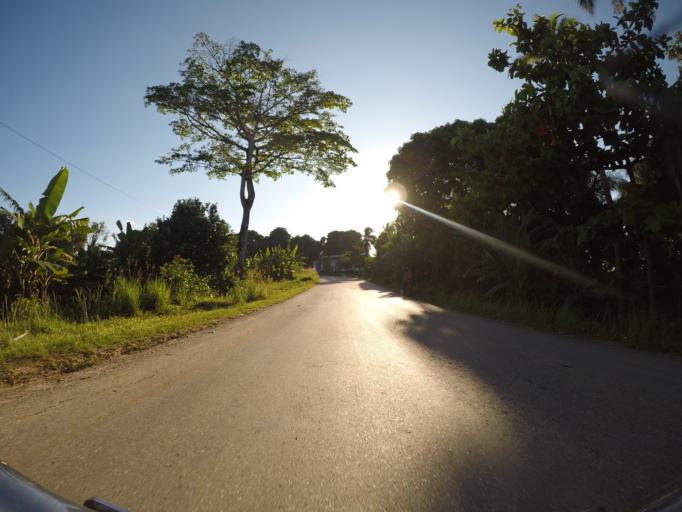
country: TZ
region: Pemba South
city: Mtambile
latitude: -5.3759
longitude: 39.7043
